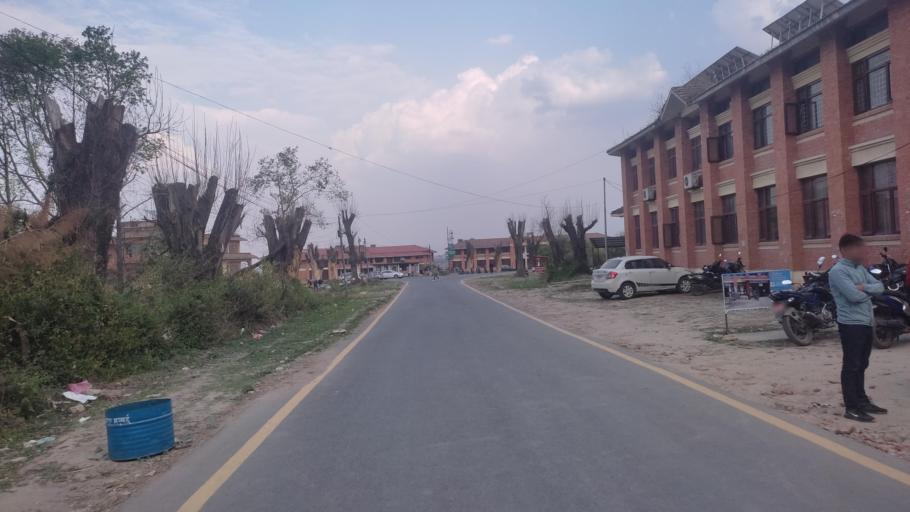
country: NP
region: Central Region
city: Kirtipur
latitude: 27.6824
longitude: 85.2865
